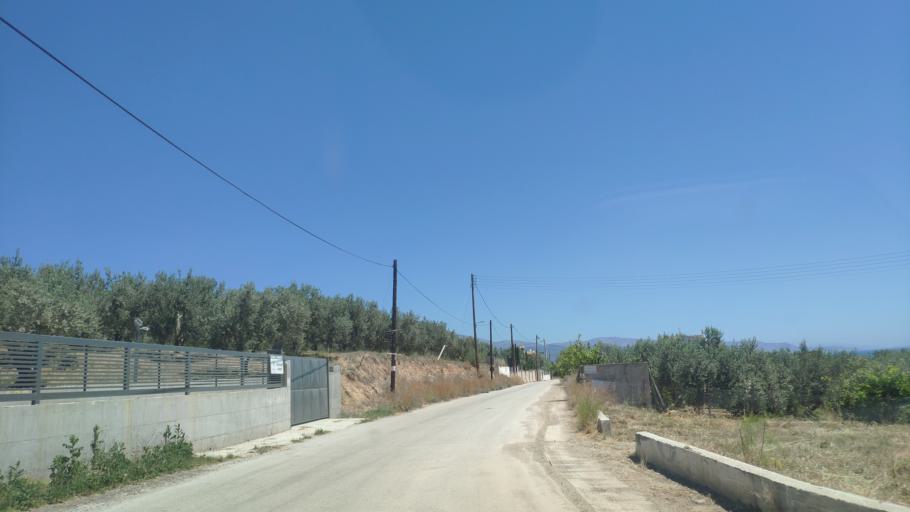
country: GR
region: Peloponnese
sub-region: Nomos Korinthias
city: Loutra Oraias Elenis
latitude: 37.8515
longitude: 22.9848
